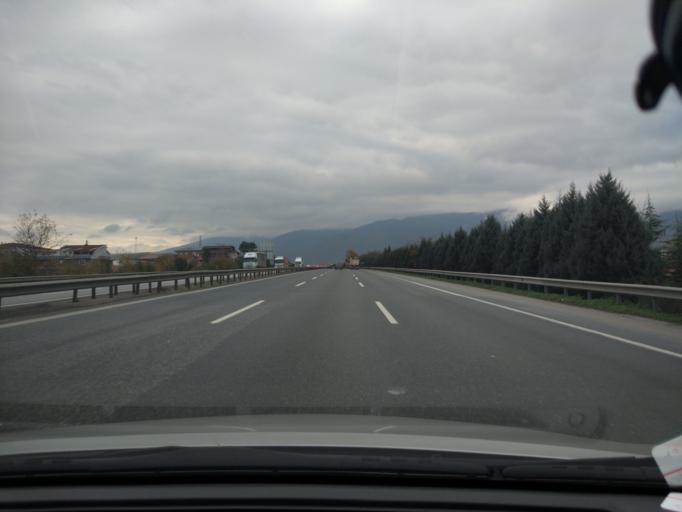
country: TR
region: Kocaeli
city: Kosekoy
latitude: 40.7384
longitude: 30.0475
